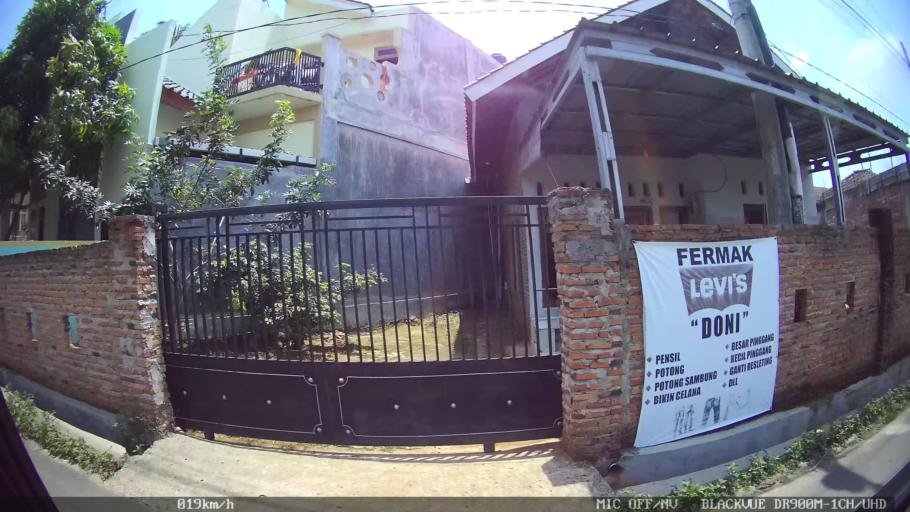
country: ID
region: Lampung
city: Kedaton
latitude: -5.3686
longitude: 105.2604
